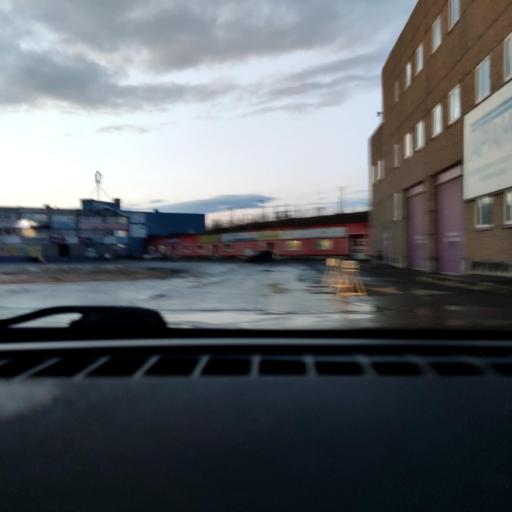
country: RU
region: Perm
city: Kondratovo
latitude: 58.0051
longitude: 56.1553
